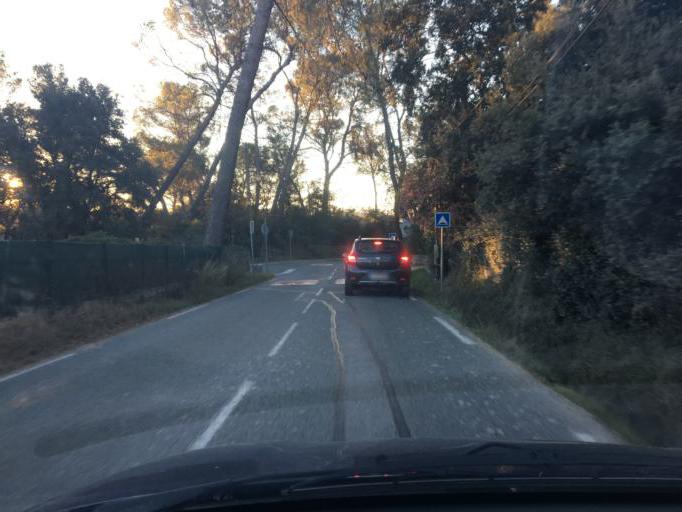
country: FR
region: Provence-Alpes-Cote d'Azur
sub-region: Departement du Var
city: Taradeau
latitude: 43.4548
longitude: 6.4224
